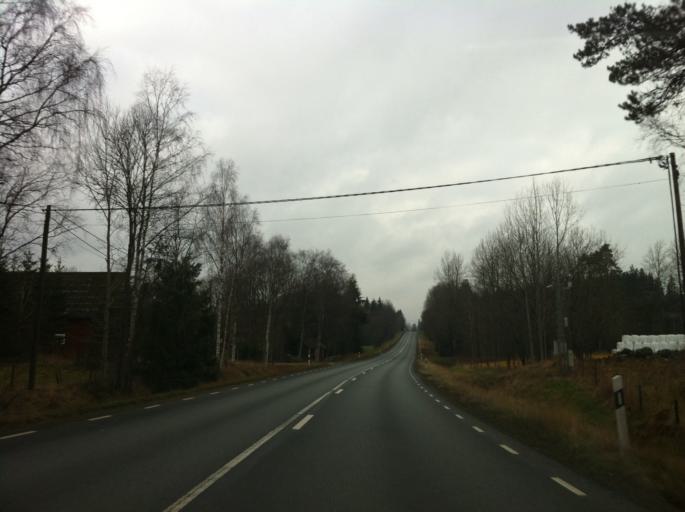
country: SE
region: Joenkoeping
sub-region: Vetlanda Kommun
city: Landsbro
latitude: 57.3880
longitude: 14.7937
